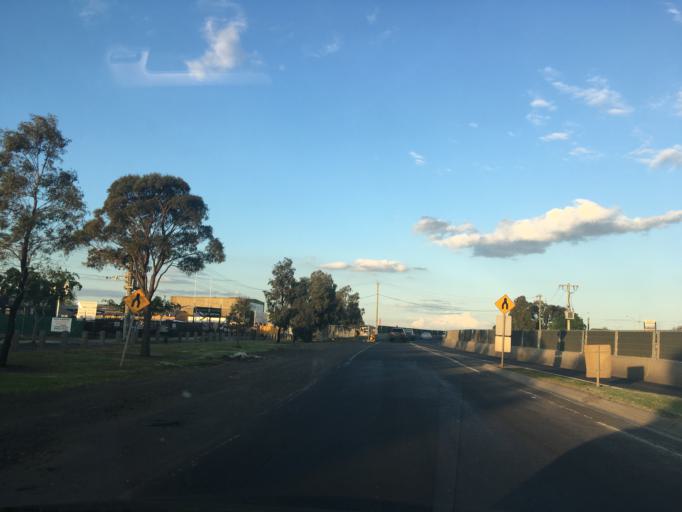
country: AU
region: Victoria
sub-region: Wyndham
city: Williams Landing
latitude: -37.8692
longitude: 144.7306
